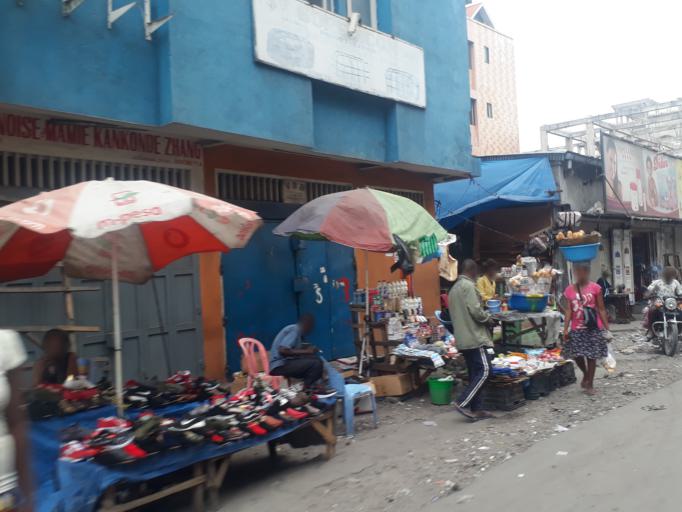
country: CD
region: Kinshasa
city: Kinshasa
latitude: -4.3124
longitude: 15.3092
